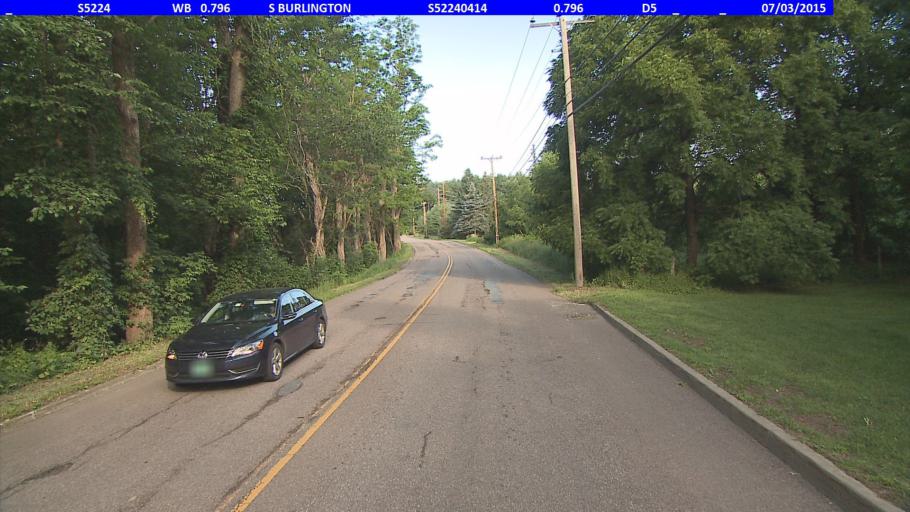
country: US
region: Vermont
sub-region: Chittenden County
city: South Burlington
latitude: 44.4447
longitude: -73.1932
